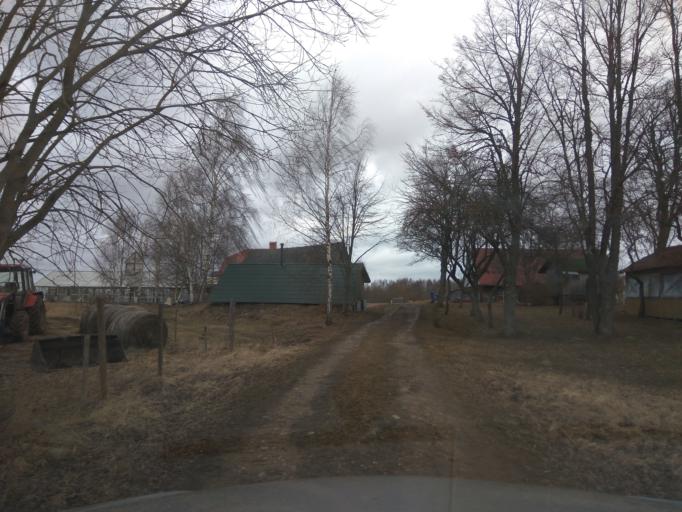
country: LV
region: Skrunda
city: Skrunda
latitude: 56.8384
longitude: 22.2097
